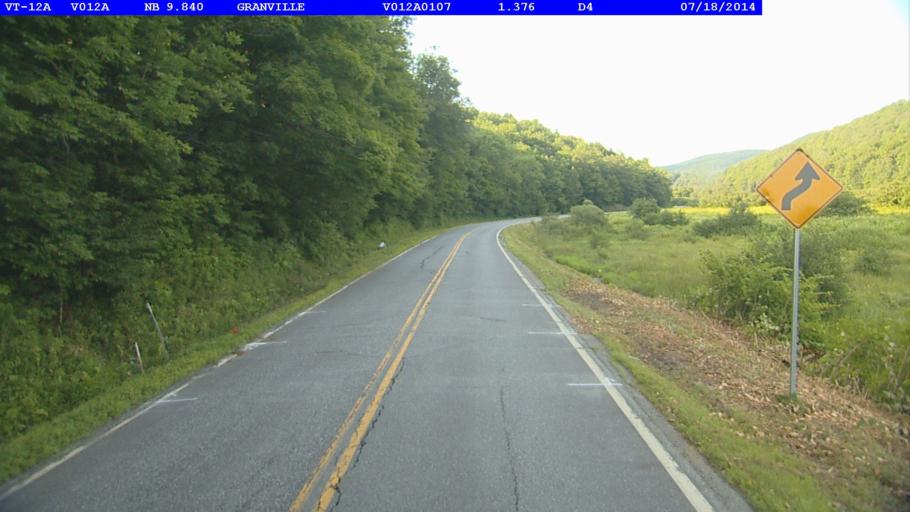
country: US
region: Vermont
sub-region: Orange County
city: Randolph
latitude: 44.0298
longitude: -72.7587
